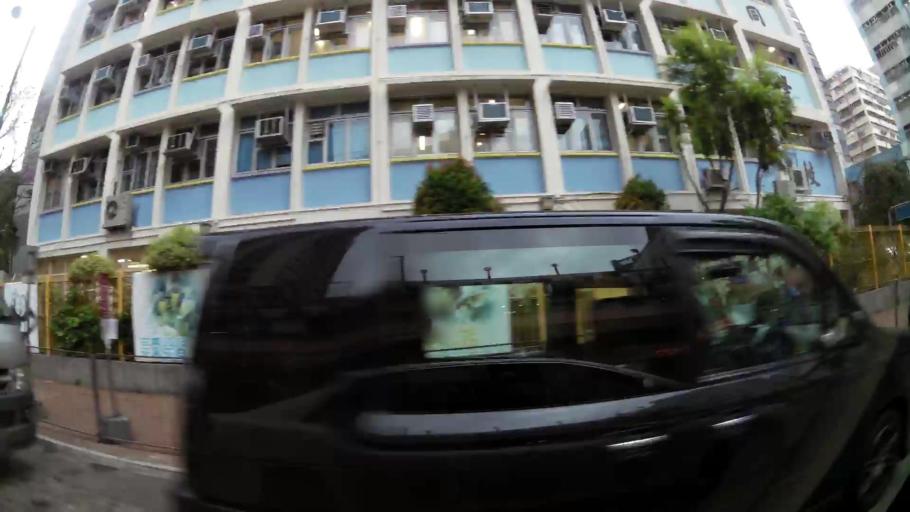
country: HK
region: Tsuen Wan
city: Tsuen Wan
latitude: 22.3640
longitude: 114.1319
